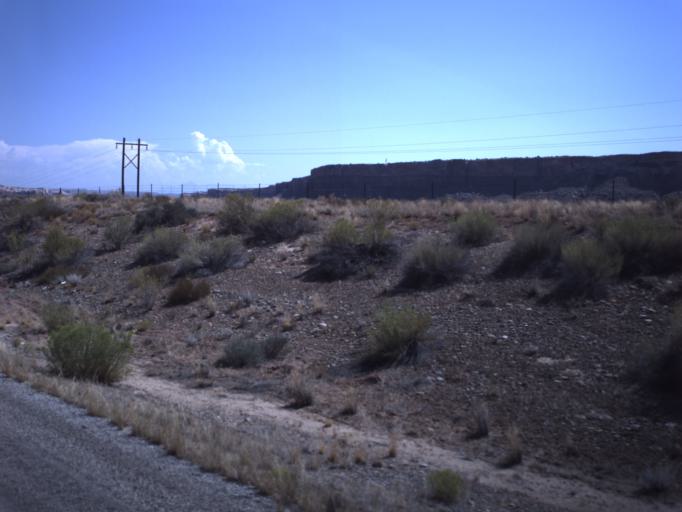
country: US
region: Utah
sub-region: San Juan County
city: Blanding
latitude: 37.2739
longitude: -109.5914
